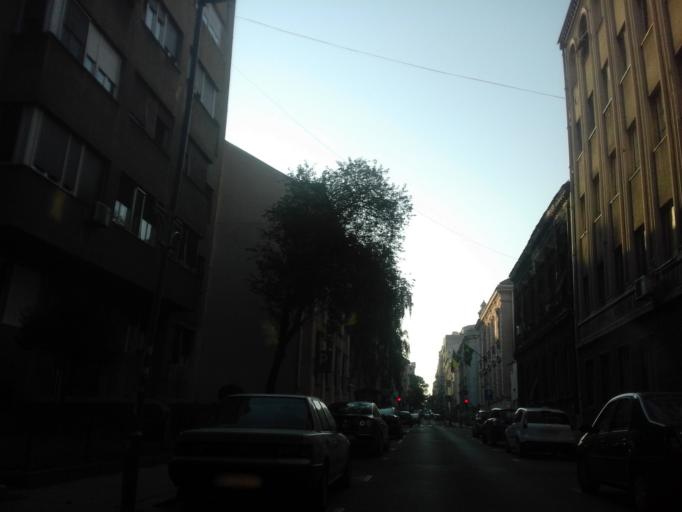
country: RS
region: Central Serbia
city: Belgrade
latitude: 44.8088
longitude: 20.4653
